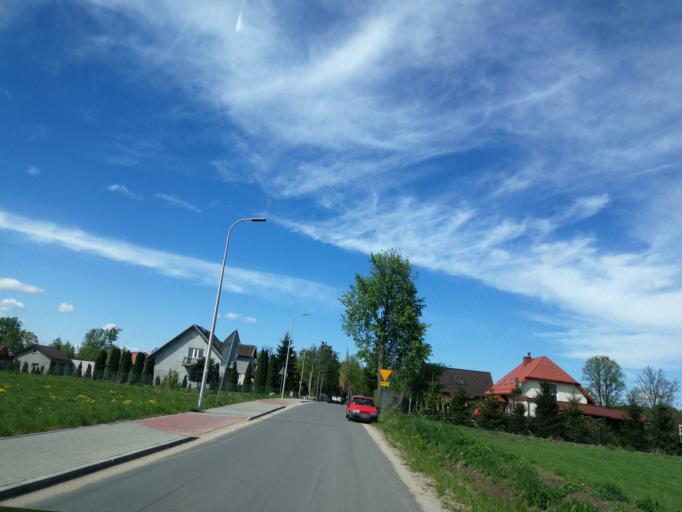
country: PL
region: Warmian-Masurian Voivodeship
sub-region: Powiat ilawski
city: Ilawa
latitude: 53.6278
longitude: 19.6655
